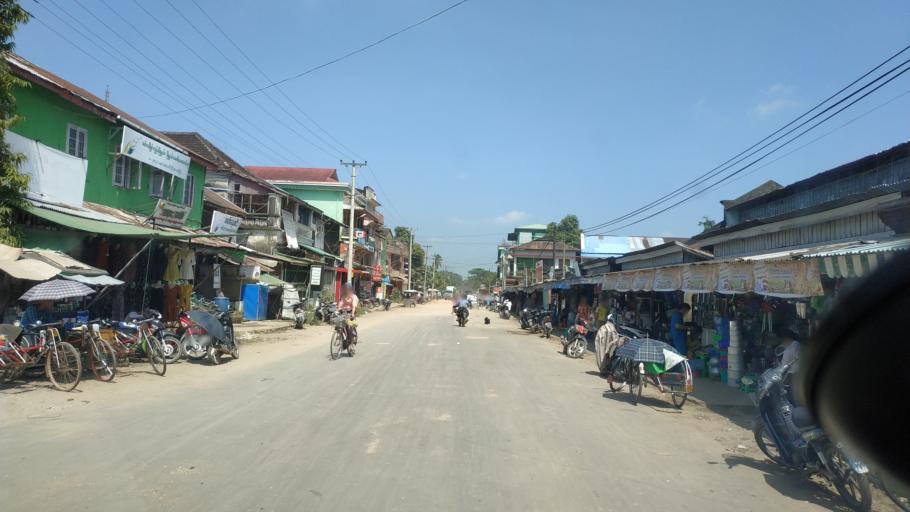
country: MM
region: Ayeyarwady
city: Mawlamyinegyunn
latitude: 16.3770
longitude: 95.2661
